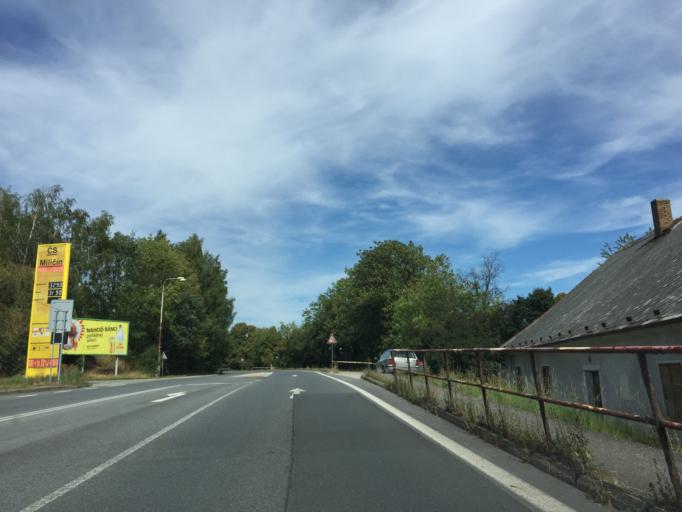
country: CZ
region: Central Bohemia
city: Votice
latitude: 49.5729
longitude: 14.6598
